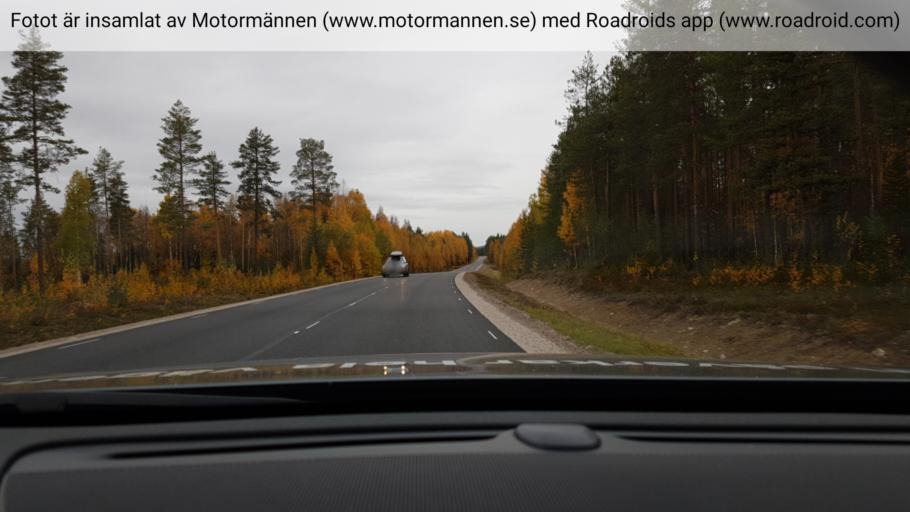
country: SE
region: Norrbotten
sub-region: Overkalix Kommun
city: OEverkalix
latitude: 66.4049
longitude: 22.8068
